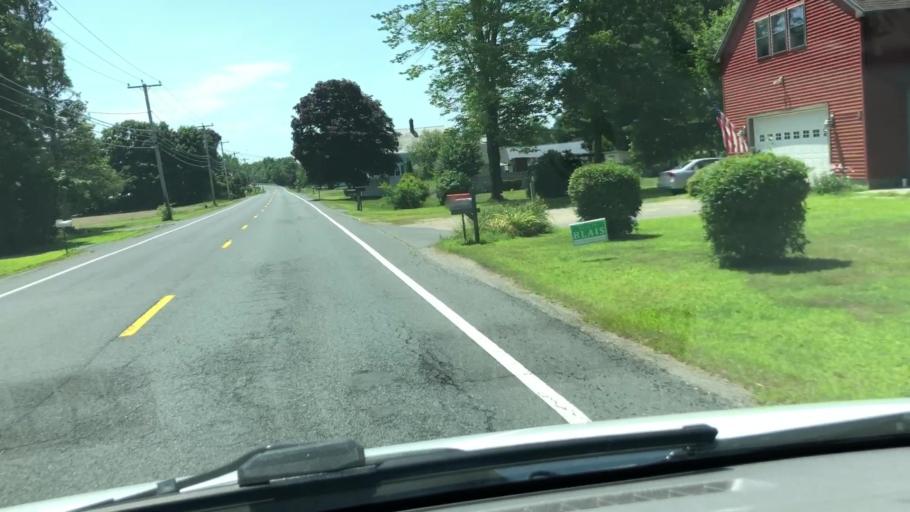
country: US
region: Massachusetts
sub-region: Franklin County
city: Whately
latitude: 42.4376
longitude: -72.6242
